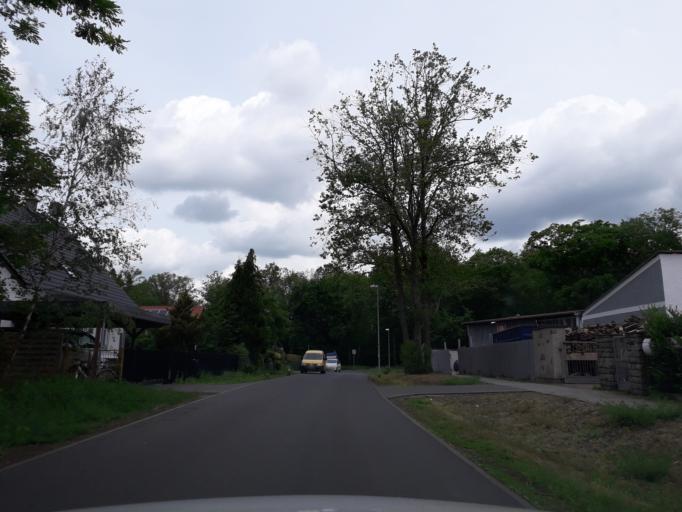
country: DE
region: Brandenburg
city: Falkensee
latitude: 52.5843
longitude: 13.0676
